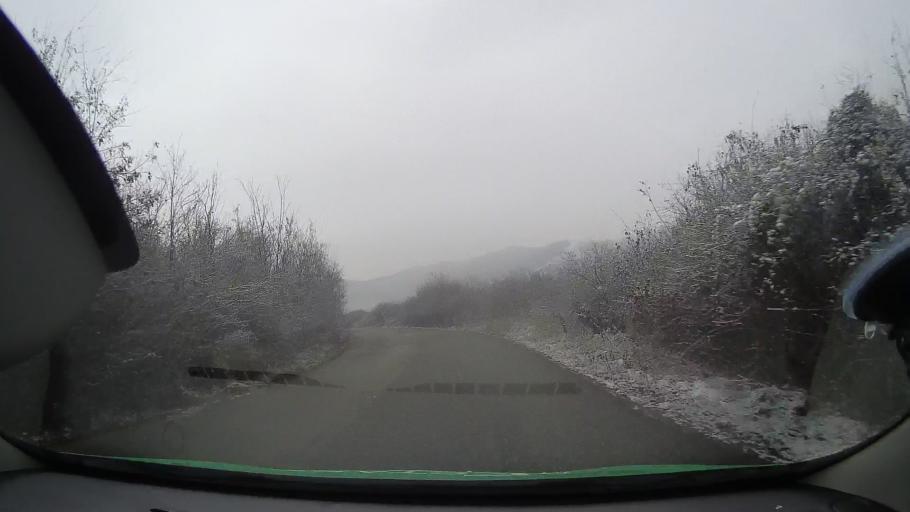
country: RO
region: Alba
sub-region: Comuna Hoparta
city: Hoparta
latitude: 46.3411
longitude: 23.9239
